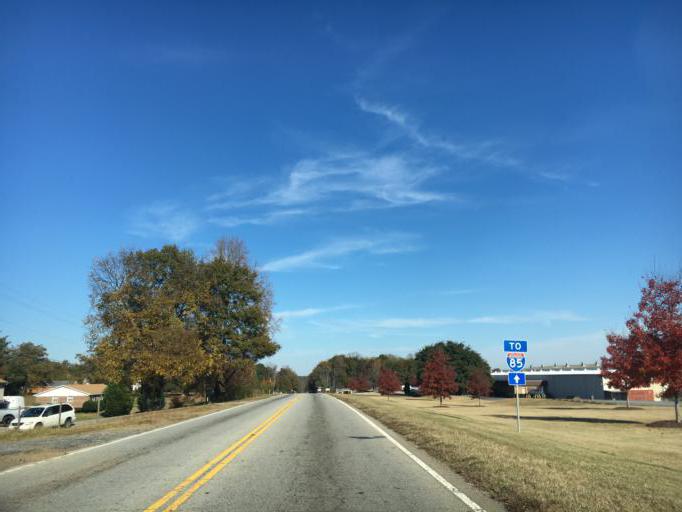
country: US
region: South Carolina
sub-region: Spartanburg County
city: Lyman
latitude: 34.9591
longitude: -82.1225
